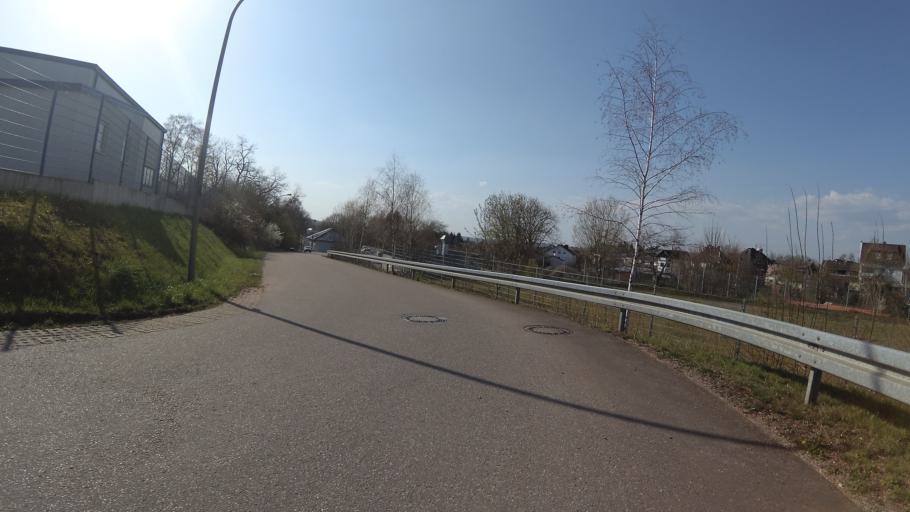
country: DE
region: Saarland
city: Heusweiler
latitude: 49.3292
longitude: 6.9387
